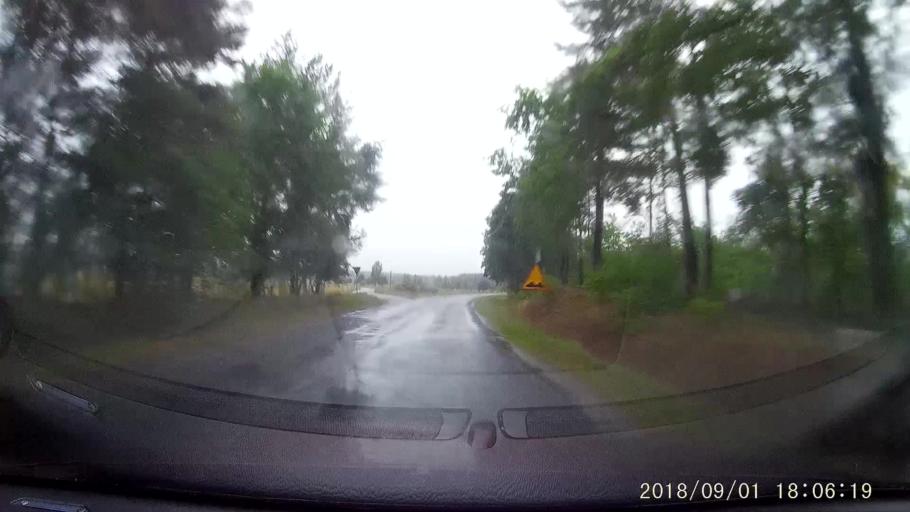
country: PL
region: Lower Silesian Voivodeship
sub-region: Powiat zgorzelecki
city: Wegliniec
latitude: 51.3560
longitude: 15.1574
